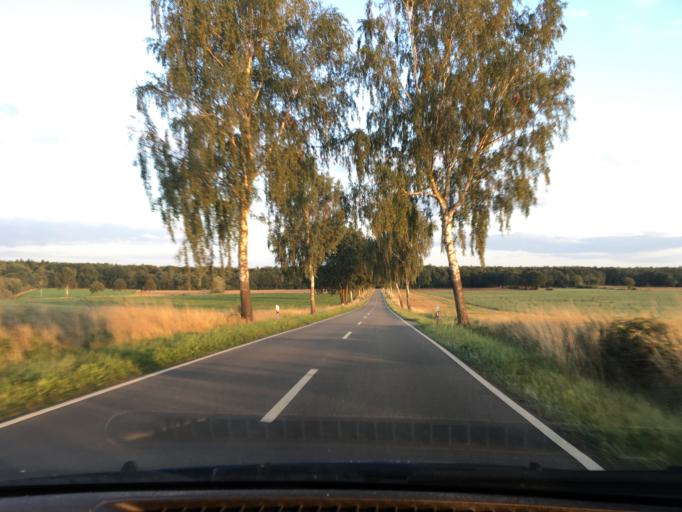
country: DE
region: Lower Saxony
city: Tosterglope
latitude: 53.2373
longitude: 10.7922
